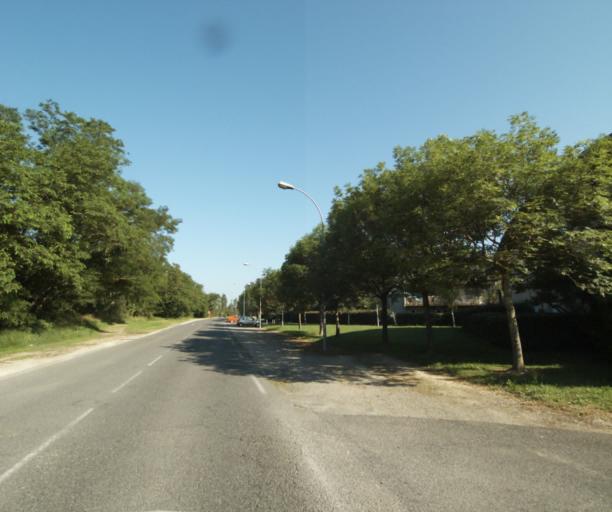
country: FR
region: Midi-Pyrenees
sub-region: Departement du Tarn-et-Garonne
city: Montauban
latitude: 44.0188
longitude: 1.3836
